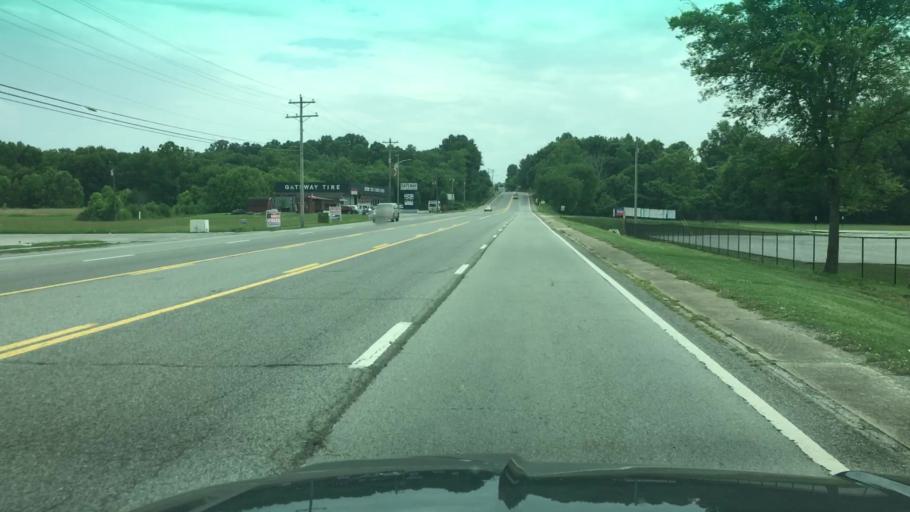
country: US
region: Tennessee
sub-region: Coffee County
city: Manchester
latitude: 35.4831
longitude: -86.0780
